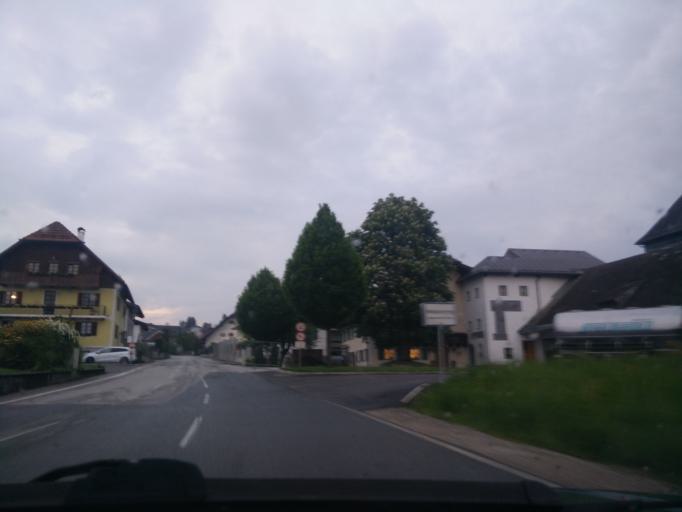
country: AT
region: Salzburg
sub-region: Politischer Bezirk Salzburg-Umgebung
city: Seekirchen am Wallersee
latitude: 47.8972
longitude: 13.1183
